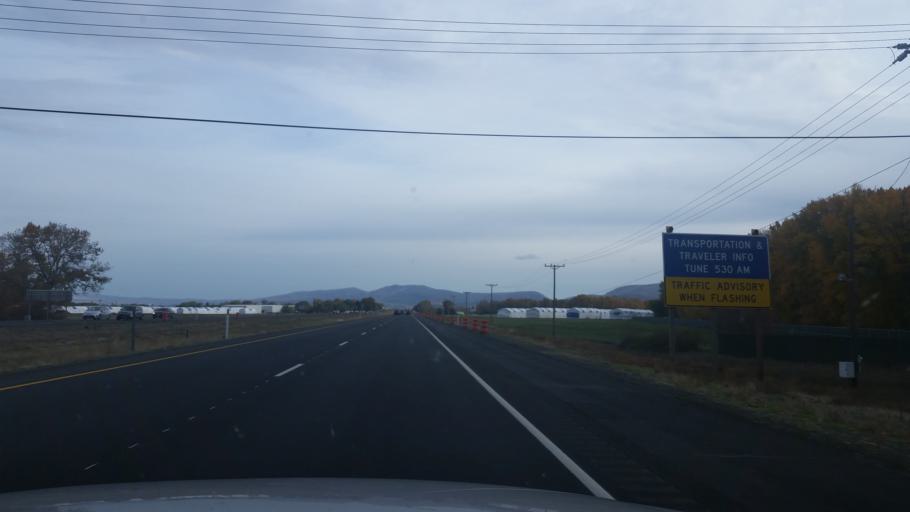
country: US
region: Washington
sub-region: Kittitas County
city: Ellensburg
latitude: 46.9889
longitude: -120.5703
